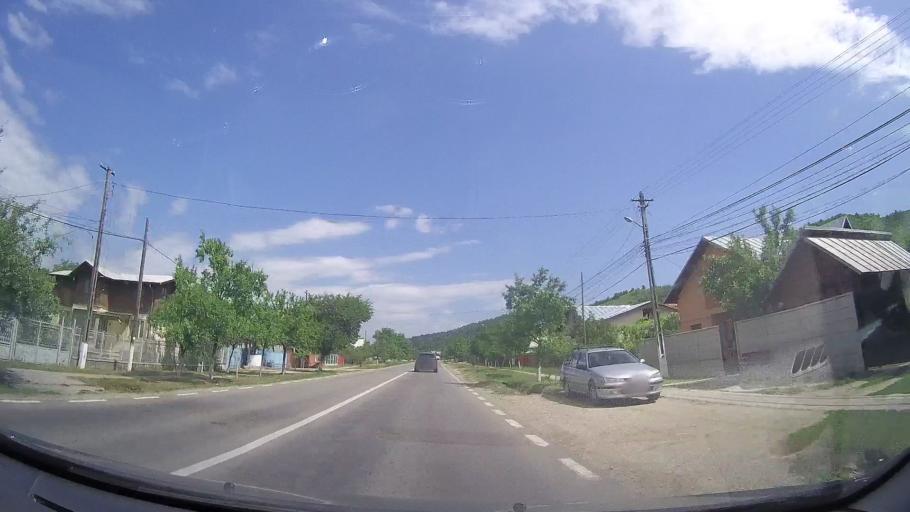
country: RO
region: Prahova
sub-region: Comuna Gura Vitioarei
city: Fagetu
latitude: 45.1213
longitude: 26.0344
